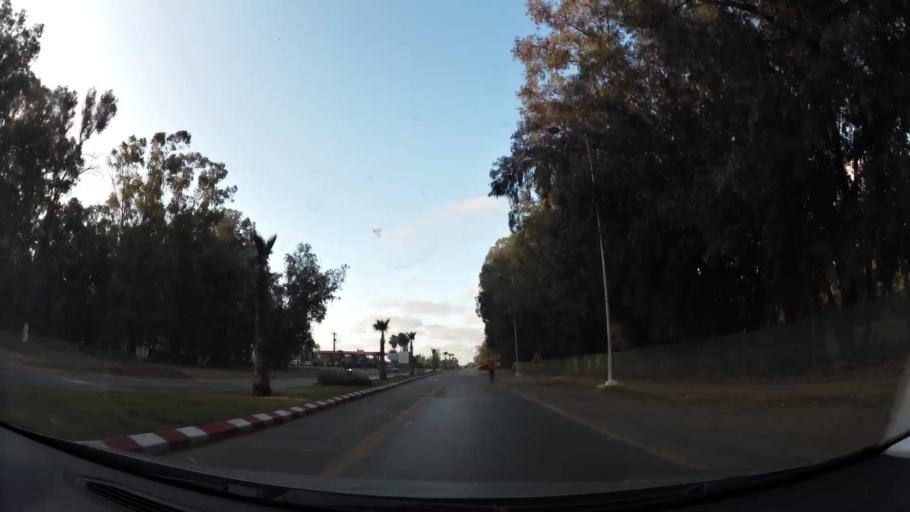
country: MA
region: Gharb-Chrarda-Beni Hssen
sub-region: Kenitra Province
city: Kenitra
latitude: 34.2026
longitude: -6.6767
